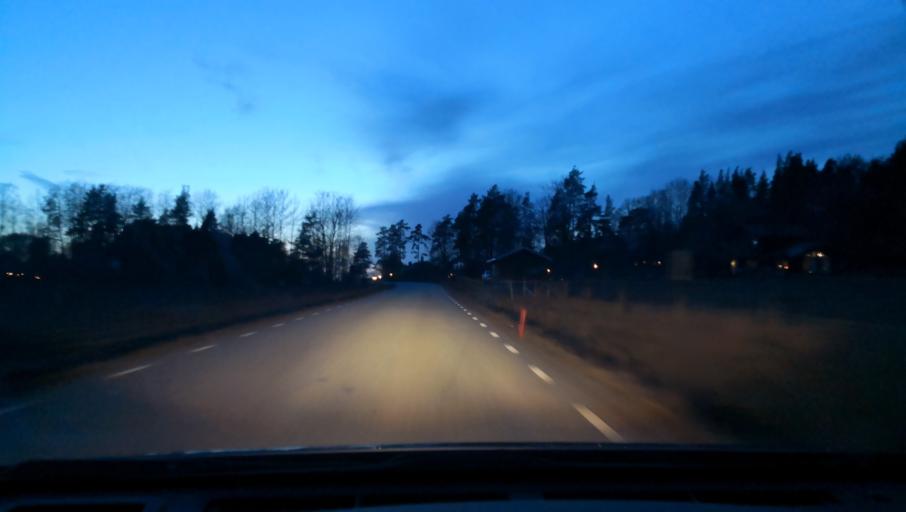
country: SE
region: Uppsala
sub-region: Enkopings Kommun
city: Grillby
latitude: 59.6067
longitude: 17.2849
